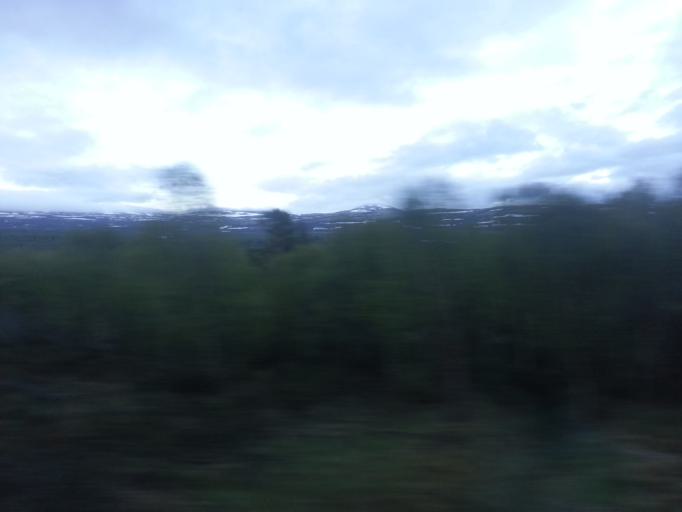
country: NO
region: Oppland
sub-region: Dovre
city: Dombas
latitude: 62.1012
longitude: 9.2058
